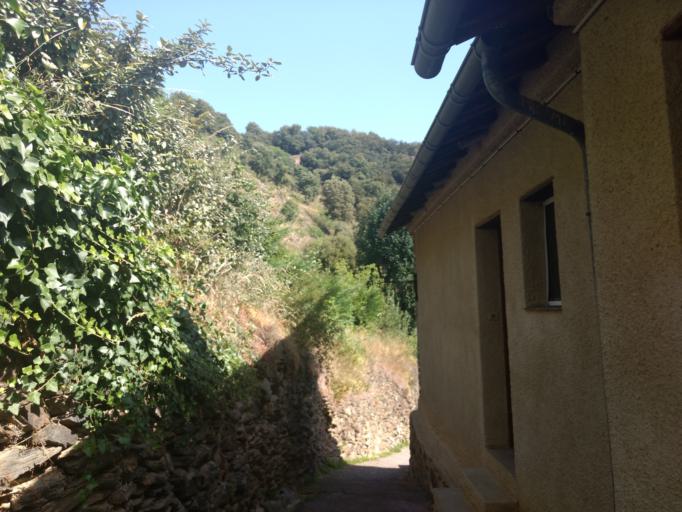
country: FR
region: Languedoc-Roussillon
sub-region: Departement des Pyrenees-Orientales
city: Vernet-les-Bains
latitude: 42.5718
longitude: 2.2955
